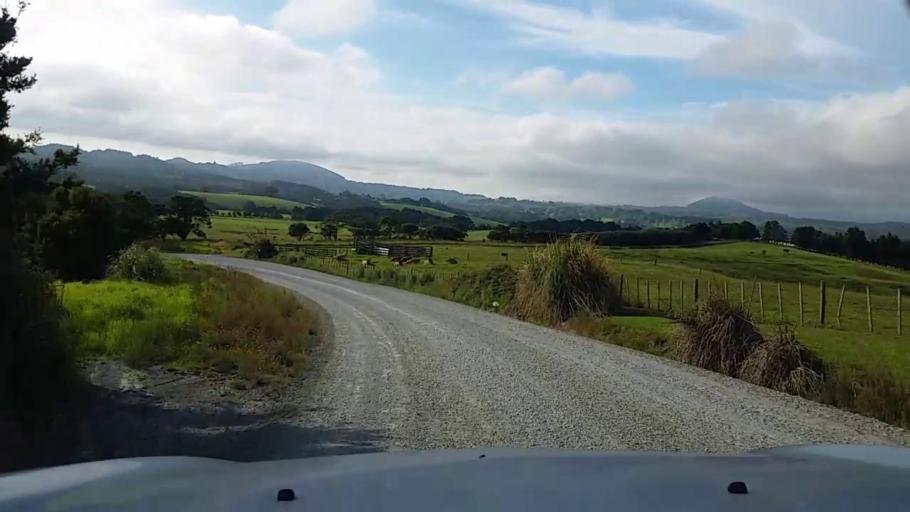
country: NZ
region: Northland
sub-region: Whangarei
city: Maungatapere
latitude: -35.6841
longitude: 174.1840
